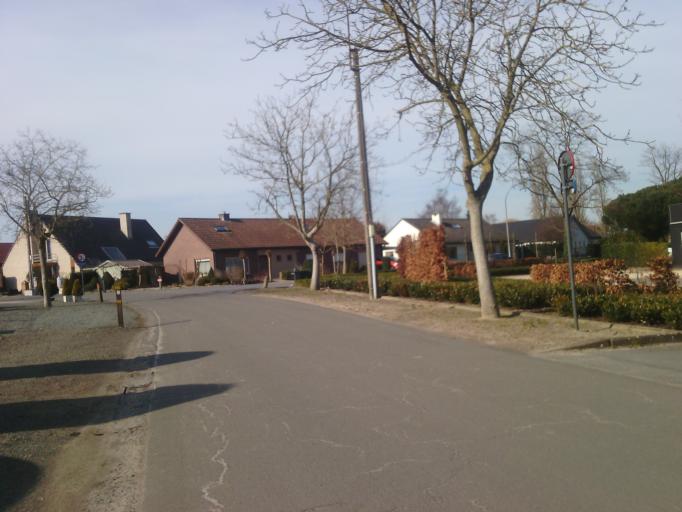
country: BE
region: Flanders
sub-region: Provincie Oost-Vlaanderen
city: Berlare
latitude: 51.0205
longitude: 3.9938
